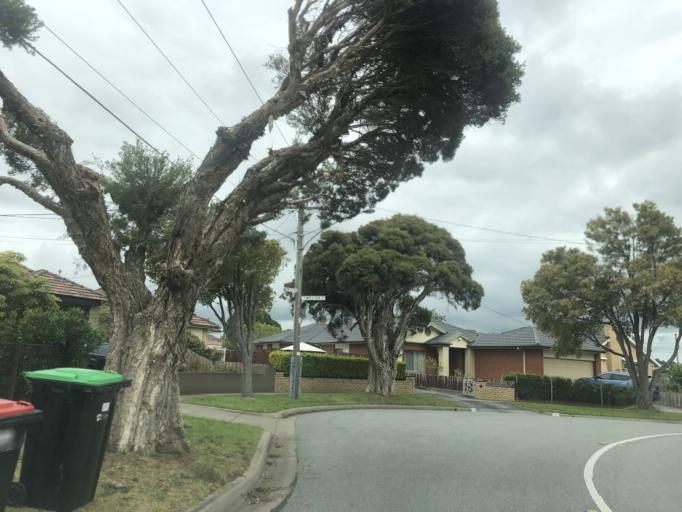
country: AU
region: Victoria
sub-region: Greater Dandenong
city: Dandenong North
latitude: -37.9668
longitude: 145.2041
